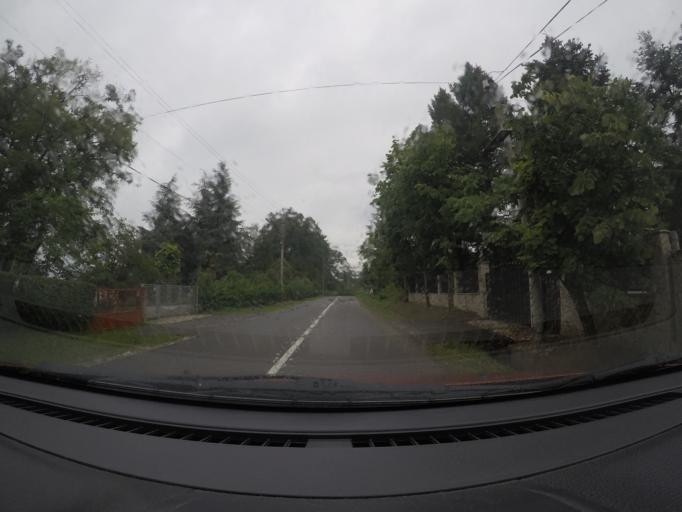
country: RS
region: Central Serbia
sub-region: Belgrade
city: Sopot
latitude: 44.5465
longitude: 20.5388
